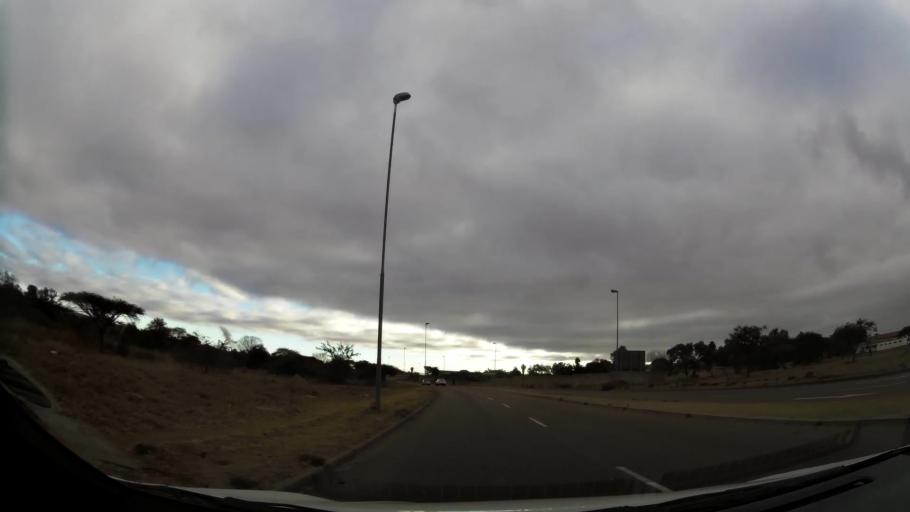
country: ZA
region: Limpopo
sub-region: Capricorn District Municipality
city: Polokwane
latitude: -23.8817
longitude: 29.4333
